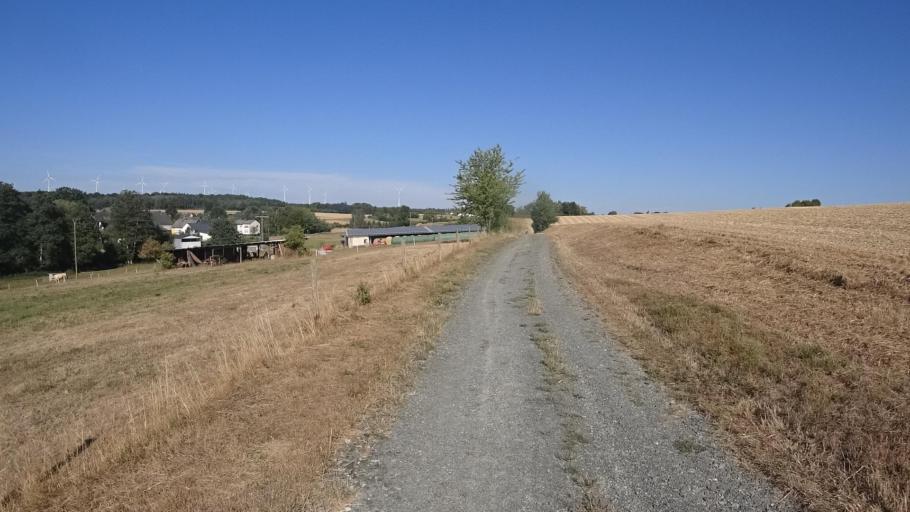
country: DE
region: Rheinland-Pfalz
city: Reich
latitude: 50.0029
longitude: 7.4357
